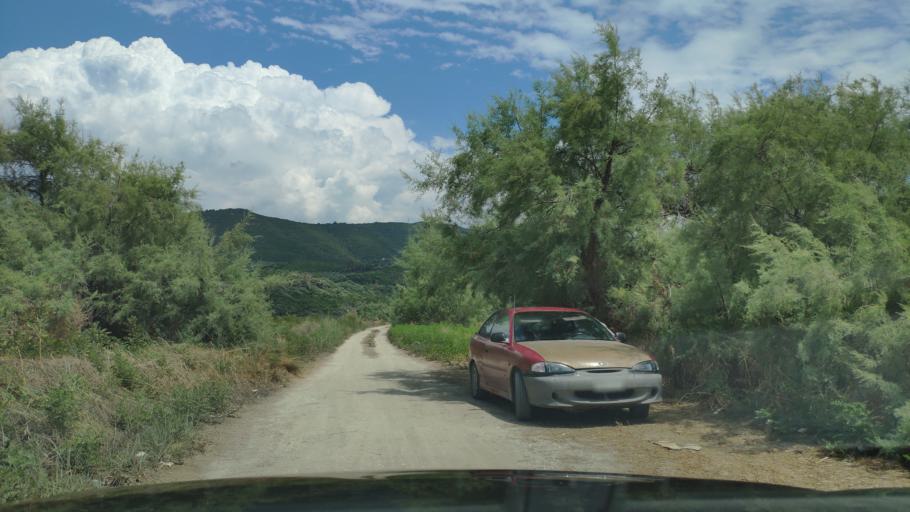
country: GR
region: West Greece
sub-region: Nomos Aitolias kai Akarnanias
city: Menidi
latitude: 39.0483
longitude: 21.0991
